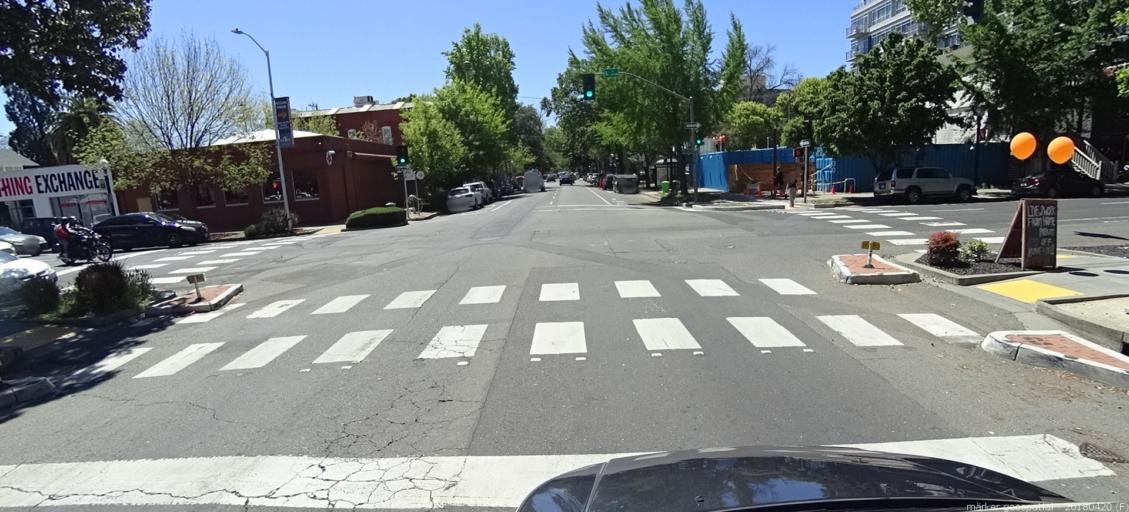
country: US
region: California
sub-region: Sacramento County
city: Sacramento
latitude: 38.5751
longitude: -121.4821
